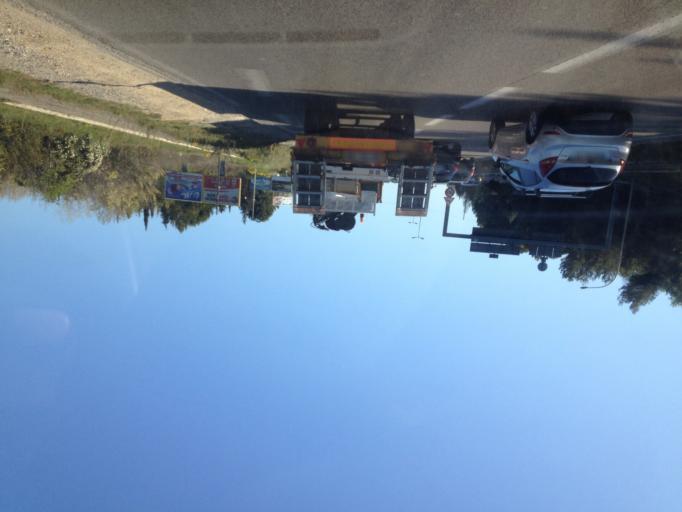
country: FR
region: Provence-Alpes-Cote d'Azur
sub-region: Departement des Bouches-du-Rhone
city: Aix-en-Provence
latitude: 43.5412
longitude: 5.4325
